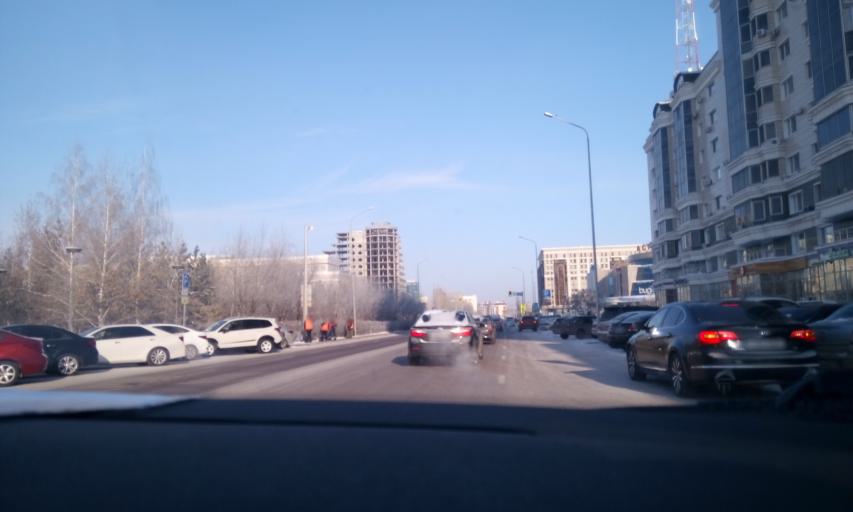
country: KZ
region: Astana Qalasy
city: Astana
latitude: 51.1288
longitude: 71.4327
